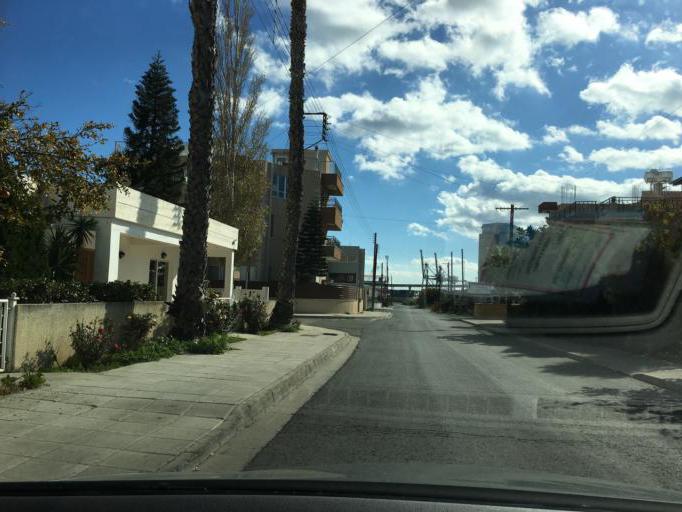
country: CY
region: Limassol
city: Limassol
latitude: 34.6577
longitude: 33.0120
